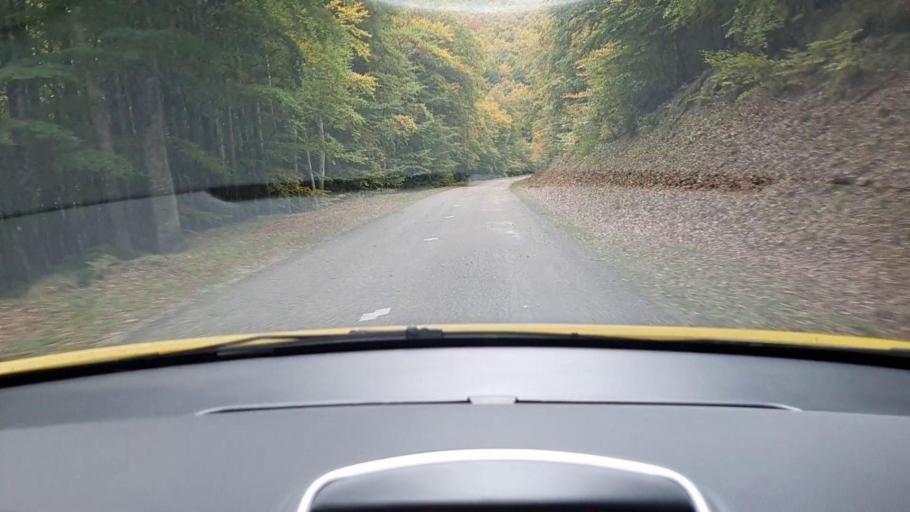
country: FR
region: Languedoc-Roussillon
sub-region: Departement de la Lozere
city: Meyrueis
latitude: 44.0912
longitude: 3.4397
